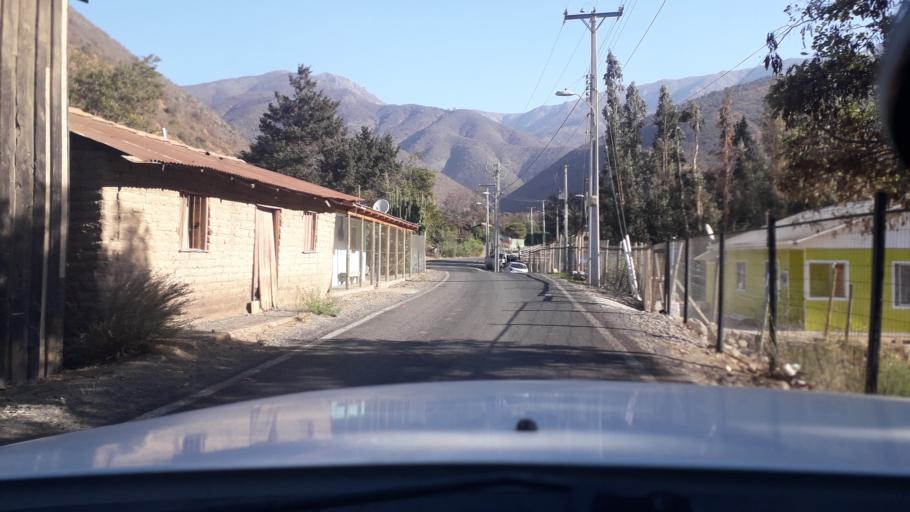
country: CL
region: Valparaiso
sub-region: Provincia de Marga Marga
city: Limache
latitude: -33.0611
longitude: -71.1167
